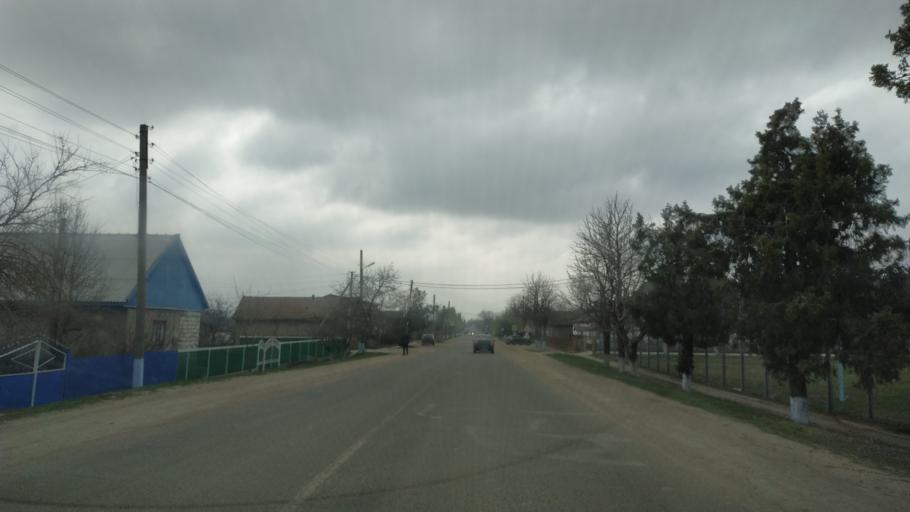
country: MD
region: Basarabeasca
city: Basarabeasca
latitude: 46.3659
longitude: 28.9320
